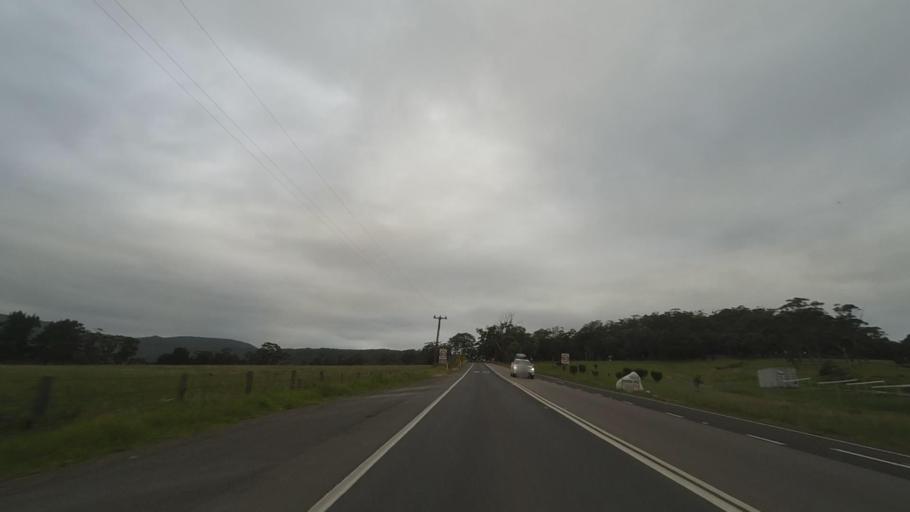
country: AU
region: New South Wales
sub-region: Kiama
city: Gerringong
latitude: -34.7400
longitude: 150.7647
